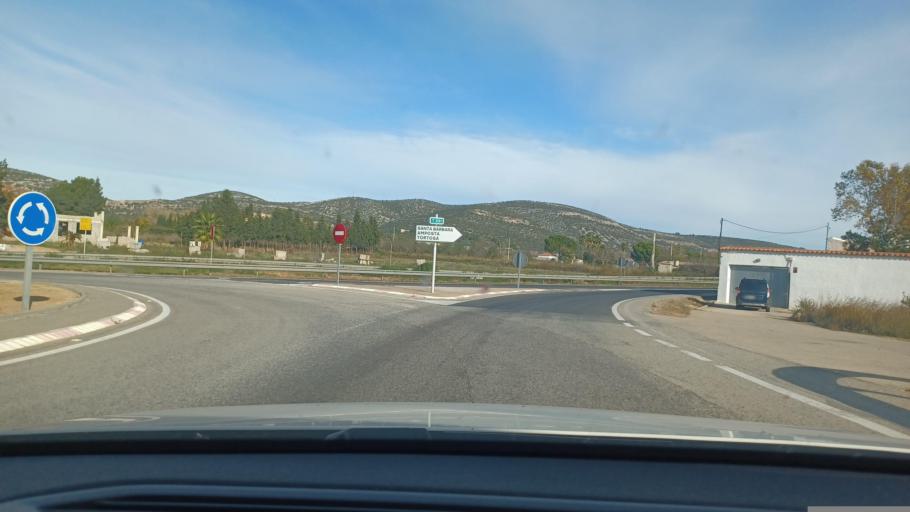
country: ES
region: Catalonia
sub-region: Provincia de Tarragona
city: Ulldecona
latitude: 40.6028
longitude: 0.4545
